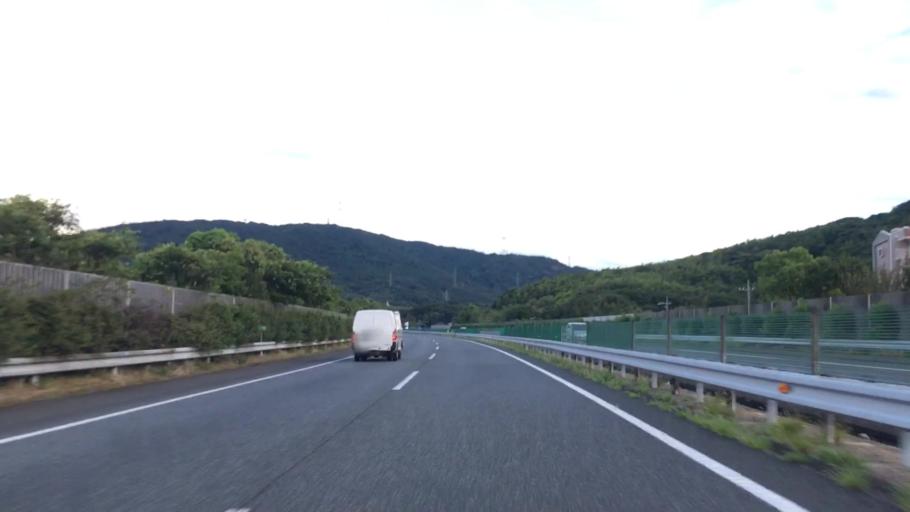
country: JP
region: Yamaguchi
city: Shimonoseki
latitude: 34.0095
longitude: 130.9558
